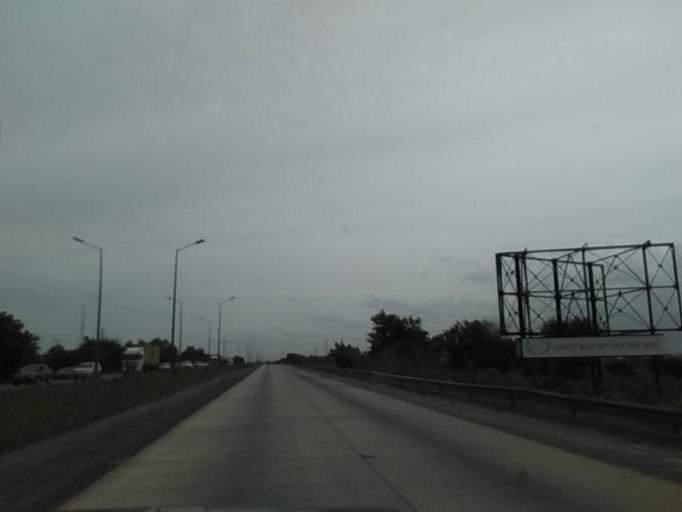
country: GH
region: Greater Accra
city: Medina Estates
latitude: 5.6491
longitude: -0.1086
